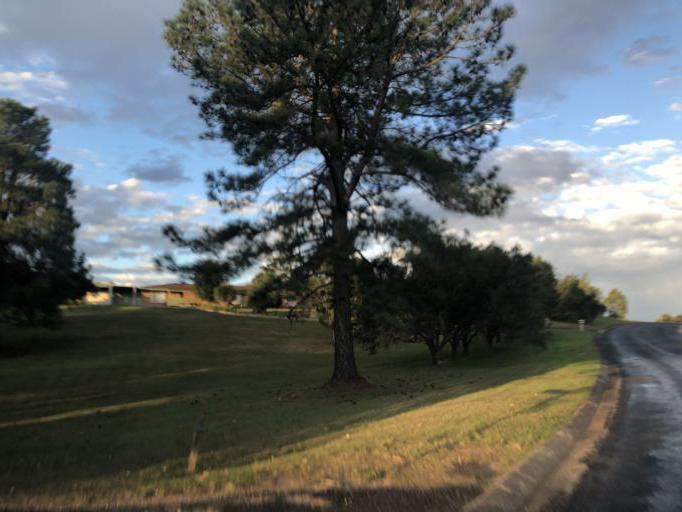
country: AU
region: New South Wales
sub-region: Nambucca Shire
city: Macksville
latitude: -30.7300
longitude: 152.9061
